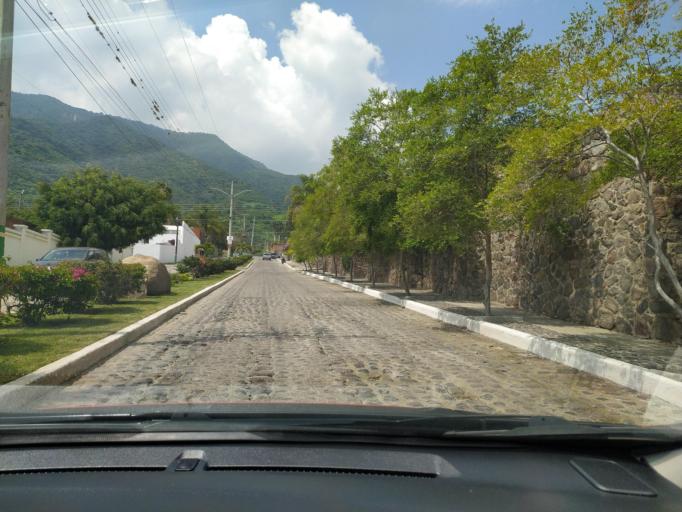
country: MX
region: Jalisco
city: San Juan Cosala
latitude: 20.2900
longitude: -103.3322
